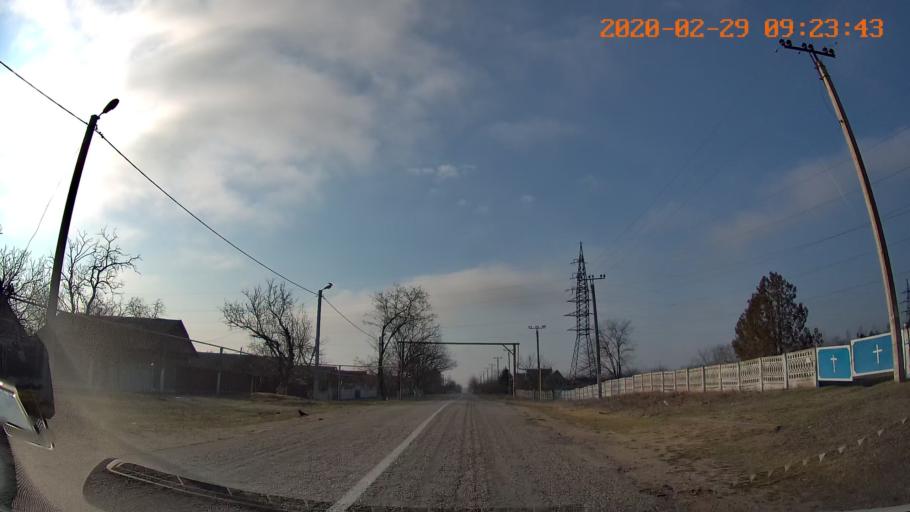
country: MD
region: Telenesti
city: Pervomaisc
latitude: 46.7230
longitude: 29.9605
